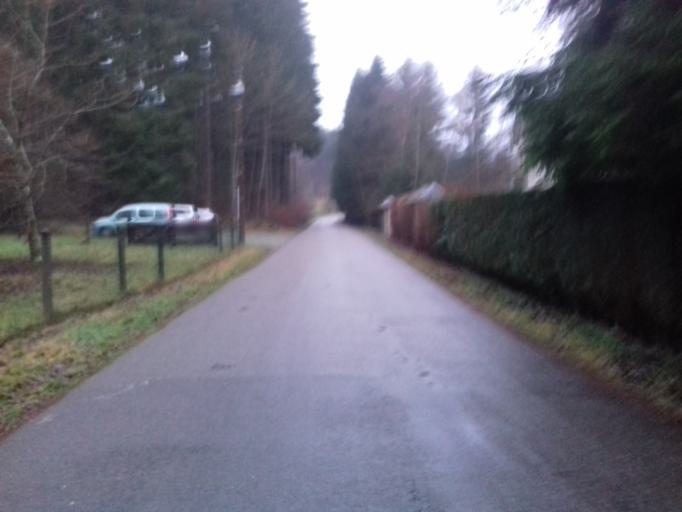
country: BE
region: Wallonia
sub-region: Province du Luxembourg
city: Libin
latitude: 49.9881
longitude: 5.3160
